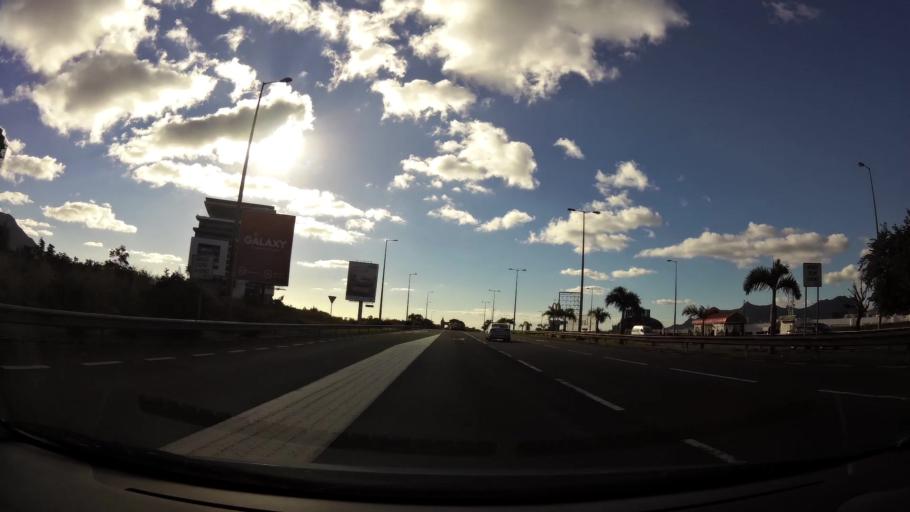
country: MU
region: Plaines Wilhems
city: Quatre Bornes
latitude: -20.2603
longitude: 57.4895
